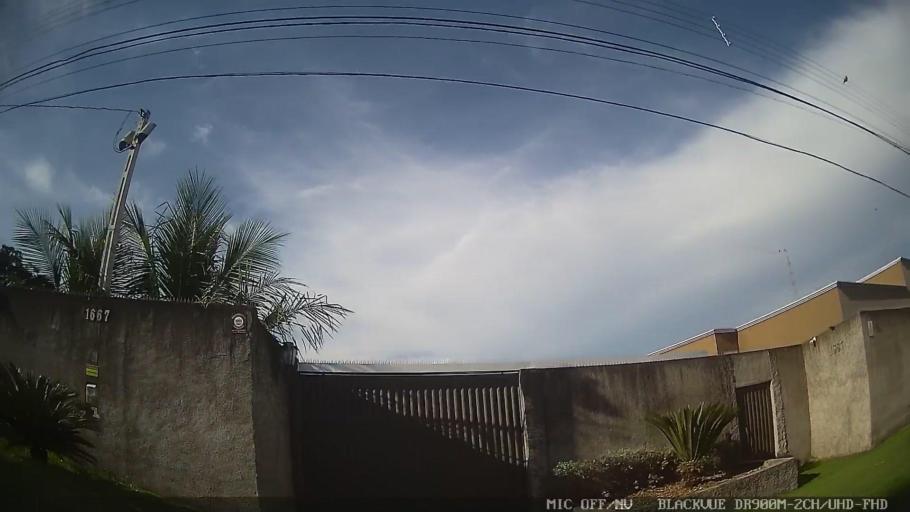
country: BR
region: Sao Paulo
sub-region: Tiete
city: Tiete
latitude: -23.0847
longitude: -47.6816
